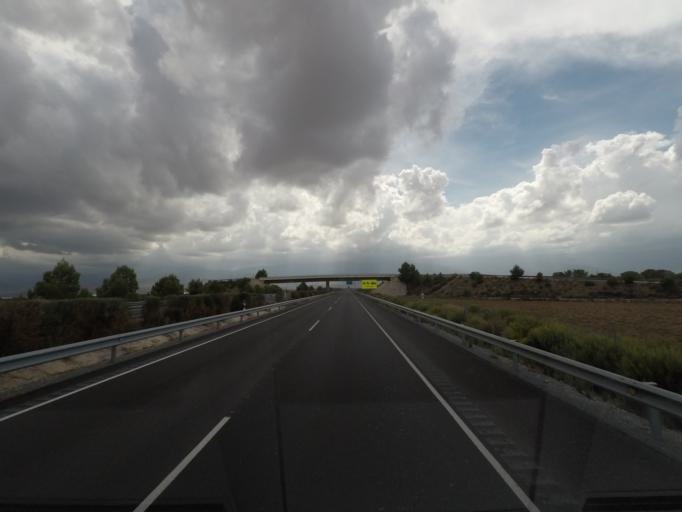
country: ES
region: Andalusia
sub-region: Provincia de Granada
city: Albunan
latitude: 37.2469
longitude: -3.0818
